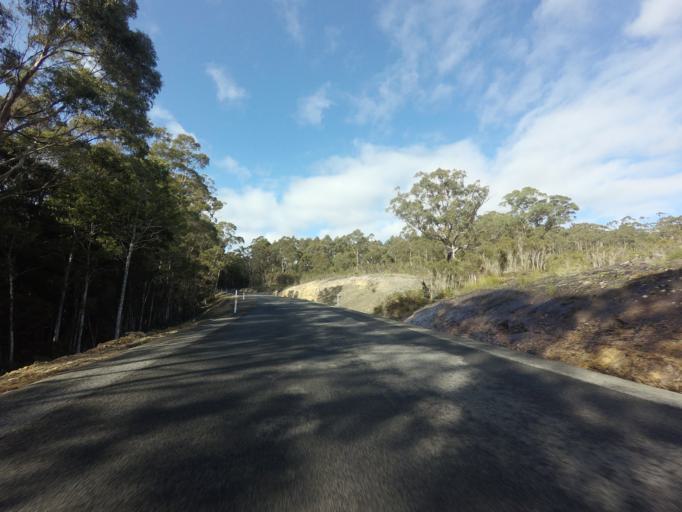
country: AU
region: Tasmania
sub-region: Huon Valley
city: Geeveston
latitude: -43.4260
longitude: 146.9056
